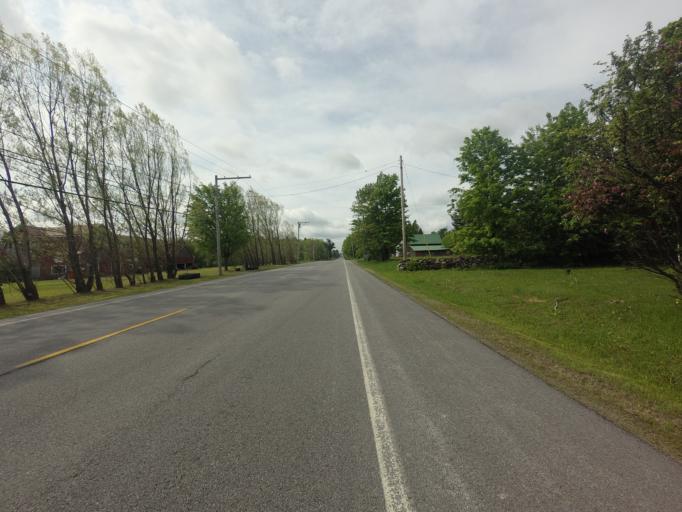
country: CA
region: Ontario
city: Cornwall
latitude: 44.7838
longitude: -74.6743
